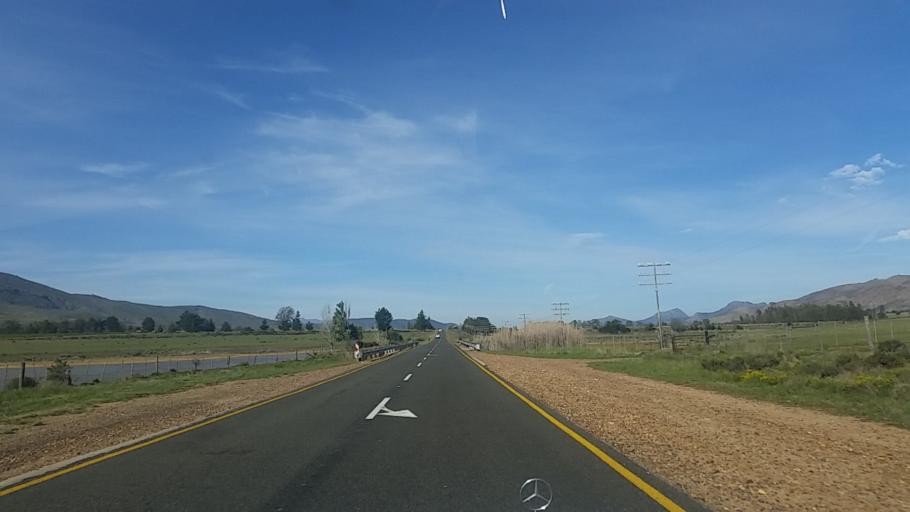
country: ZA
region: Western Cape
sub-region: Eden District Municipality
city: George
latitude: -33.8313
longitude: 22.4591
